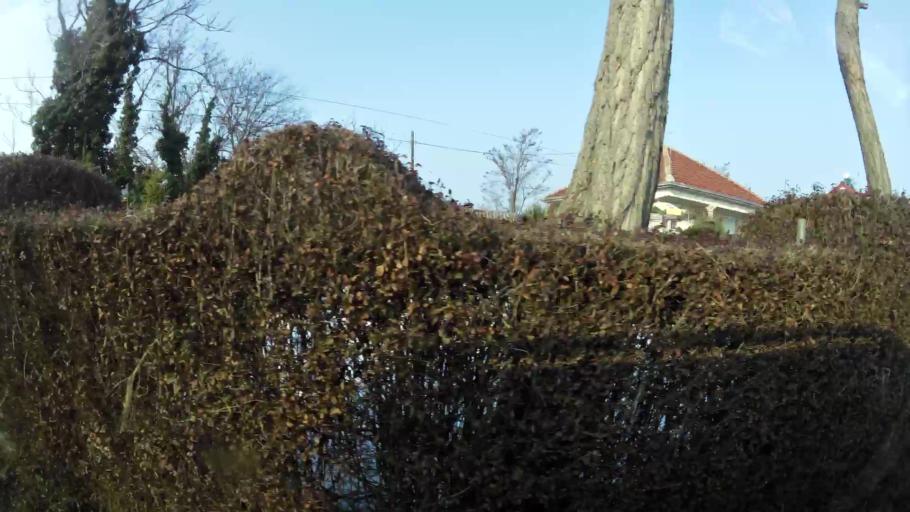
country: MK
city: Kadino
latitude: 41.9670
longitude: 21.6024
